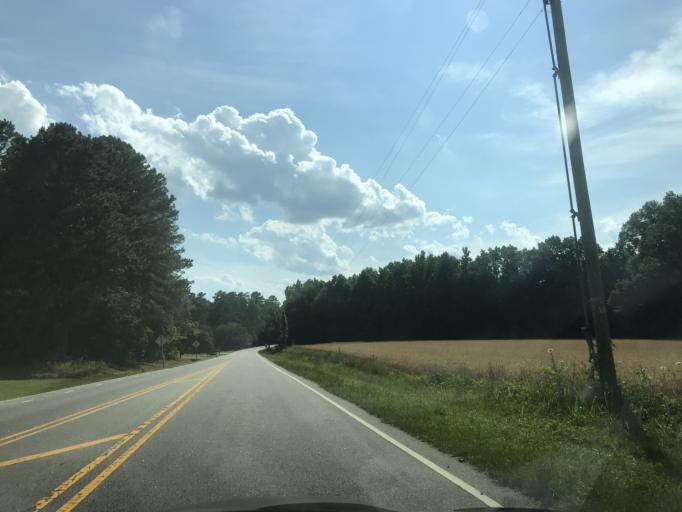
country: US
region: North Carolina
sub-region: Nash County
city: Nashville
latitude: 35.9696
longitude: -78.0200
